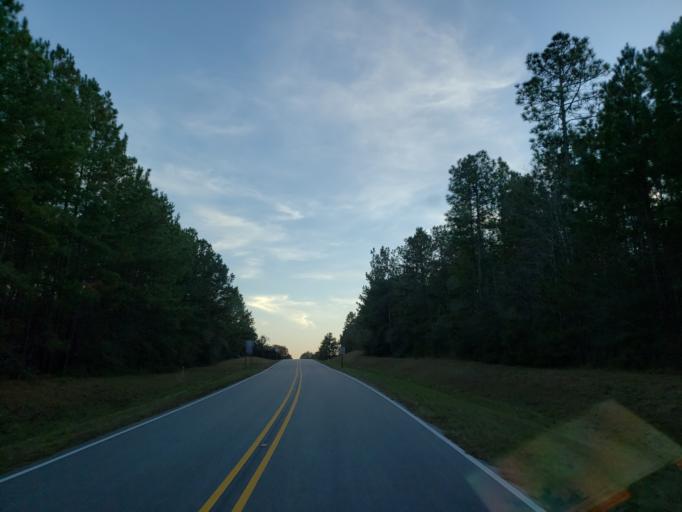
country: US
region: Mississippi
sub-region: Forrest County
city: Hattiesburg
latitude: 31.2598
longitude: -89.3140
